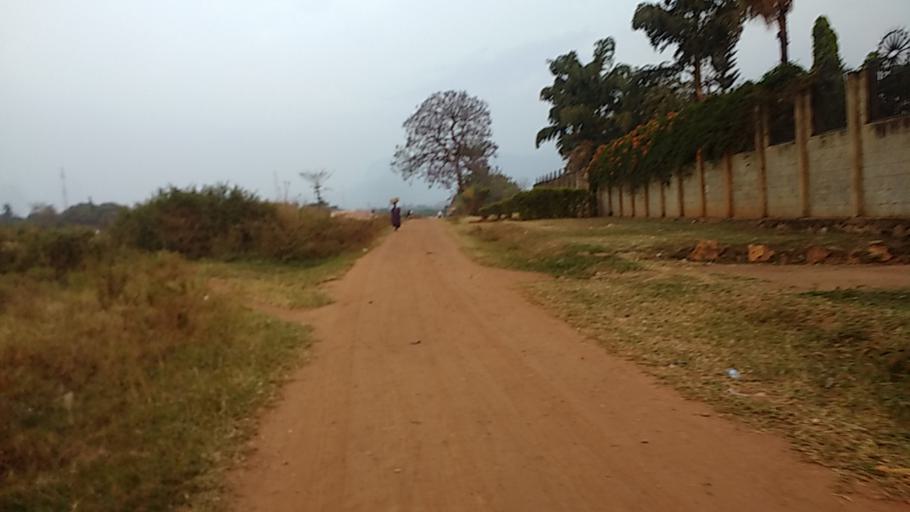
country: UG
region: Eastern Region
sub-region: Mbale District
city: Mbale
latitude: 1.0682
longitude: 34.1673
